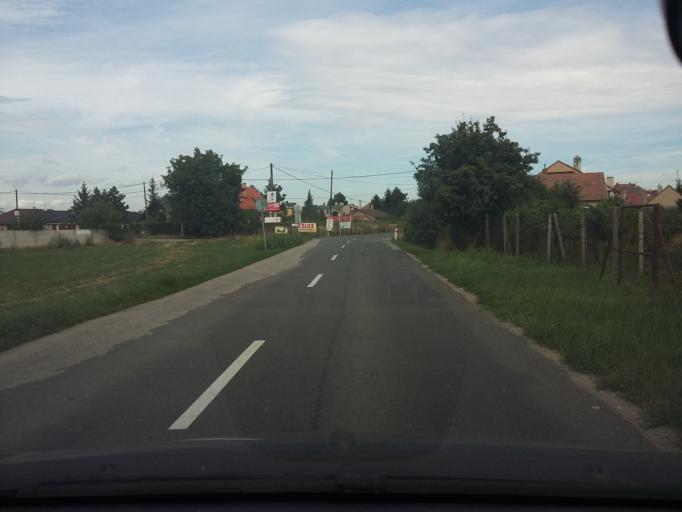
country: SK
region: Bratislavsky
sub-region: Okres Pezinok
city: Pezinok
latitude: 48.2662
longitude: 17.3019
